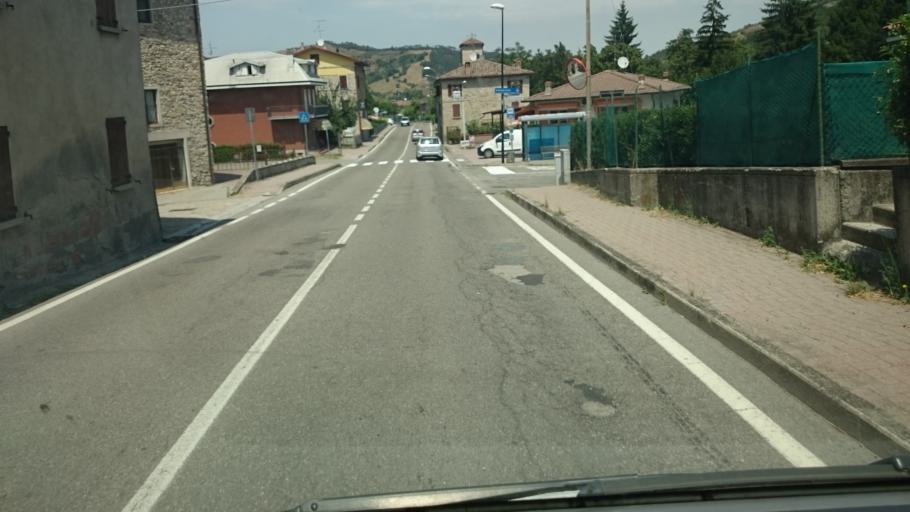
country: IT
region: Emilia-Romagna
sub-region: Provincia di Reggio Emilia
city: Vezzano sul Crostolo
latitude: 44.5663
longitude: 10.5287
